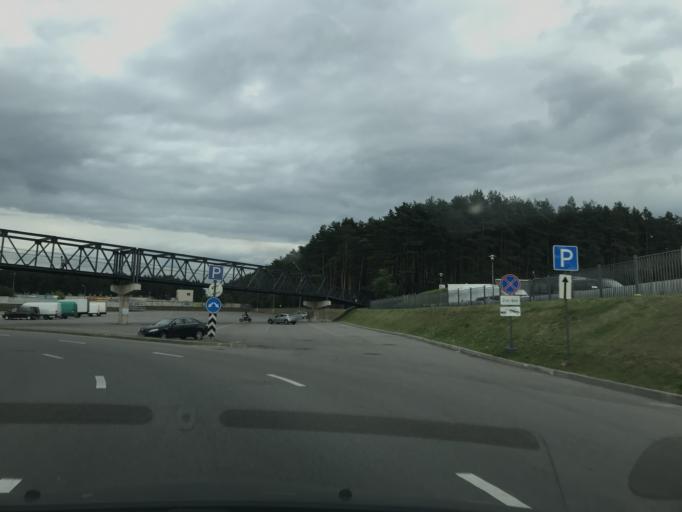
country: BY
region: Minsk
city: Borovlyany
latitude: 53.9625
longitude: 27.6298
